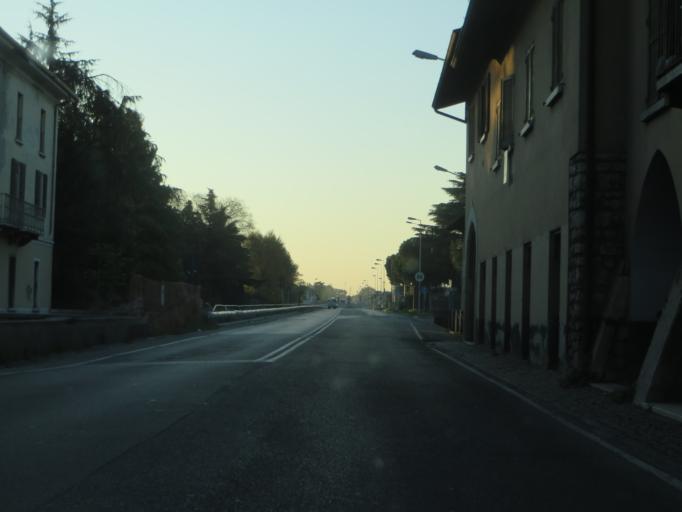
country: IT
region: Lombardy
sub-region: Provincia di Brescia
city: Rezzato
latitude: 45.5117
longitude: 10.3130
